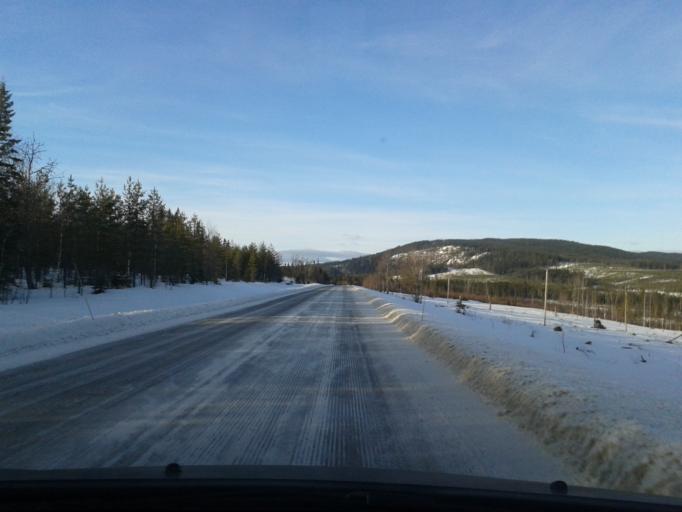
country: SE
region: Vaesterbotten
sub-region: Asele Kommun
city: Asele
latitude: 63.7747
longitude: 17.6745
